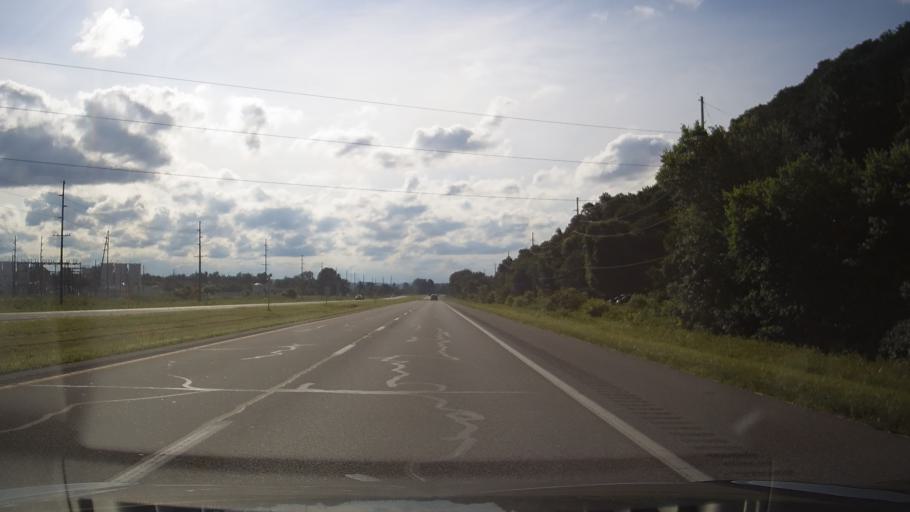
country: US
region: Kentucky
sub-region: Greenup County
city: Greenup
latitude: 38.5779
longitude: -82.7864
